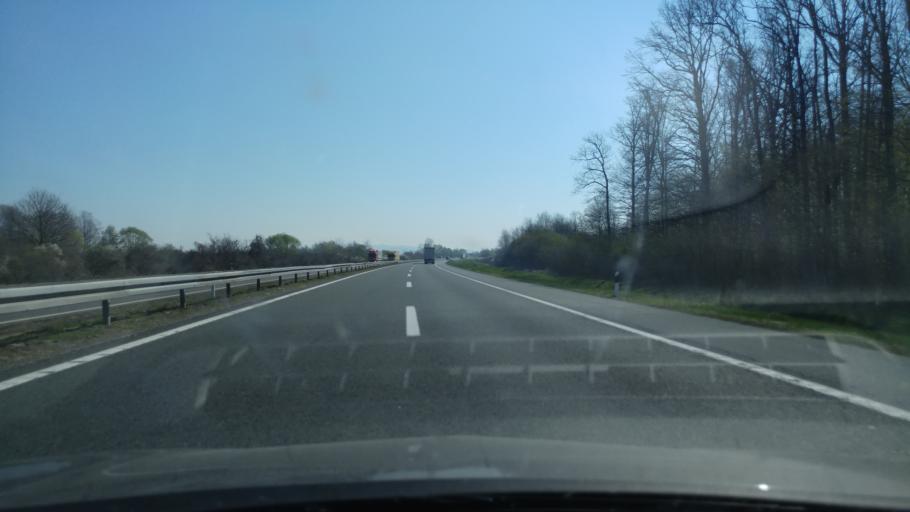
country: HR
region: Brodsko-Posavska
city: Vrbova
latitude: 45.1918
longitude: 17.6162
